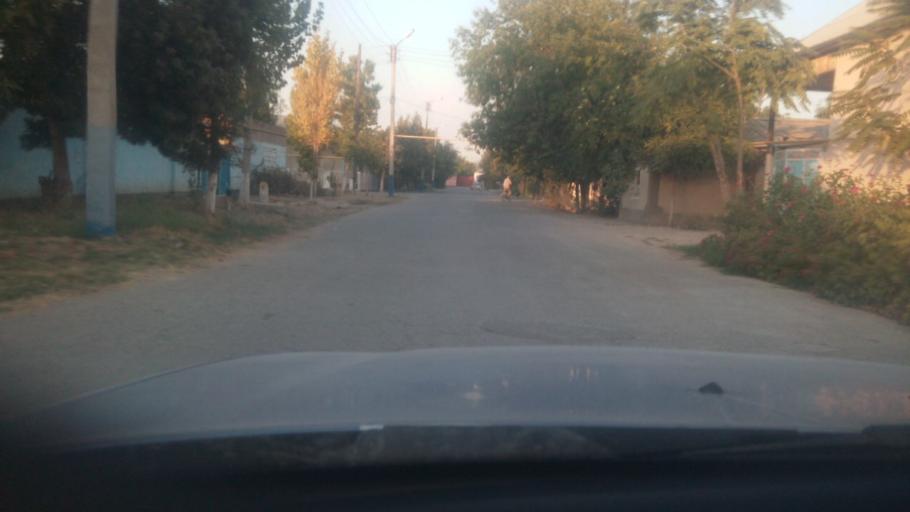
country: UZ
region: Sirdaryo
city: Guliston
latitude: 40.5019
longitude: 68.7792
